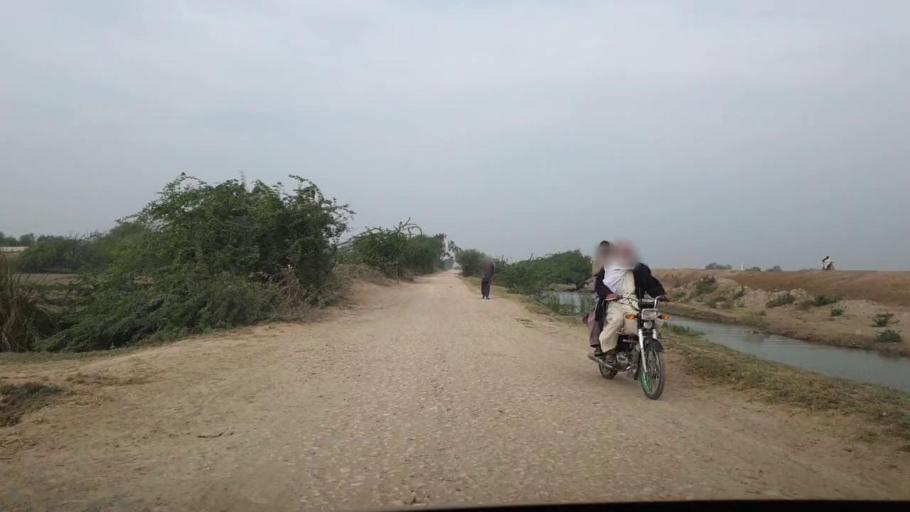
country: PK
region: Sindh
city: Chuhar Jamali
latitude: 24.4114
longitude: 67.9460
